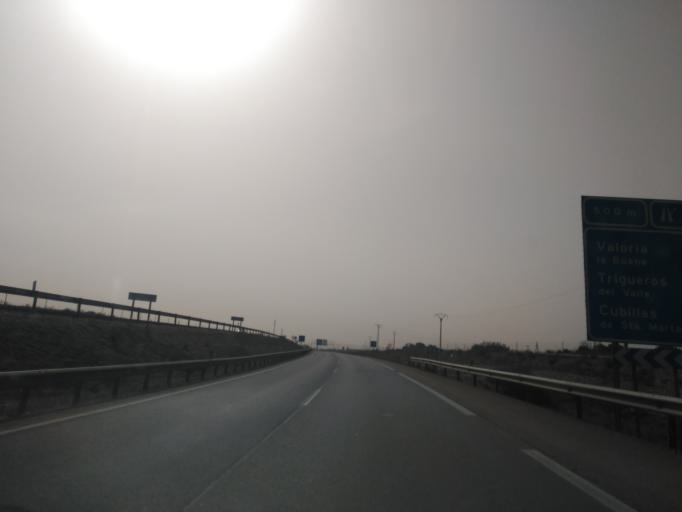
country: ES
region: Castille and Leon
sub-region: Provincia de Valladolid
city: Cubillas de Santa Marta
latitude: 41.8175
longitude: -4.5807
